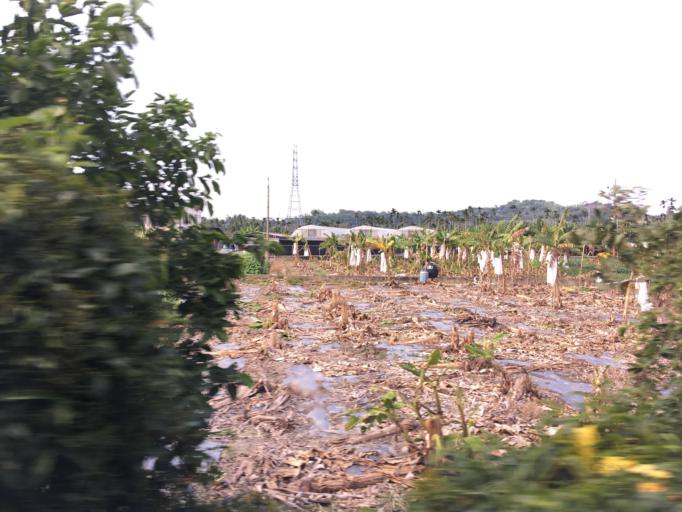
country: TW
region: Taiwan
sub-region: Chiayi
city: Jiayi Shi
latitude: 23.5026
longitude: 120.5292
